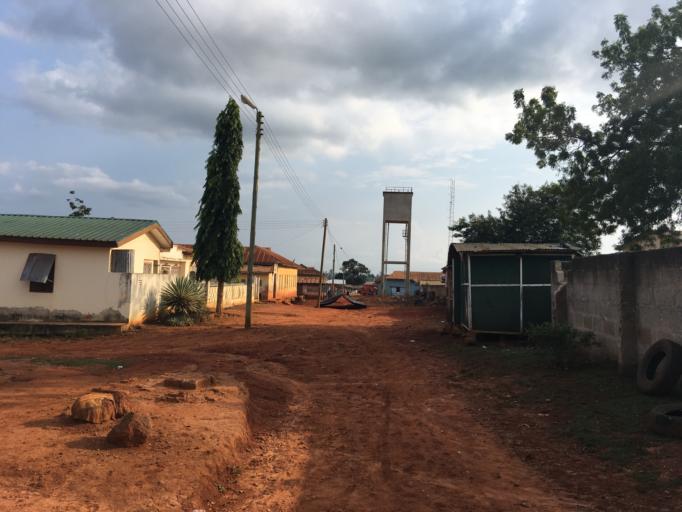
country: GH
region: Western
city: Bibiani
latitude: 6.8054
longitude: -2.5202
